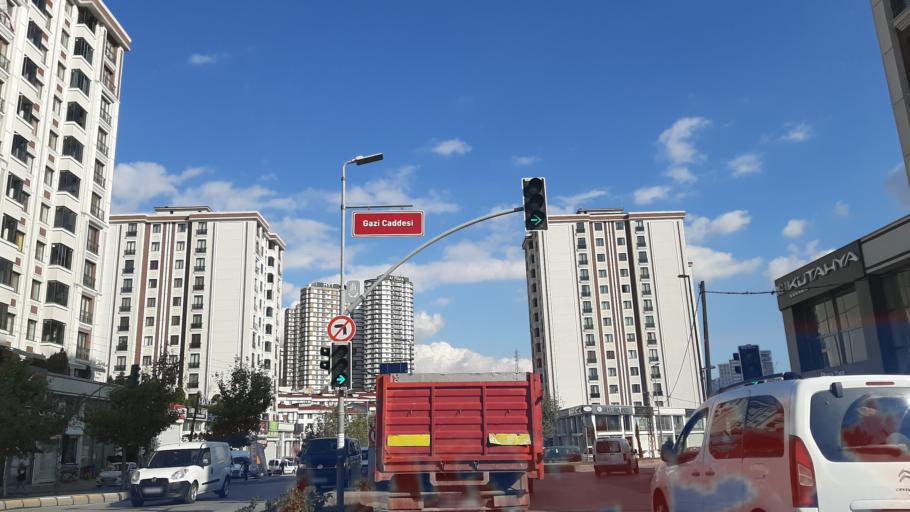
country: TR
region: Istanbul
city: Esenyurt
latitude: 41.0304
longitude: 28.6629
